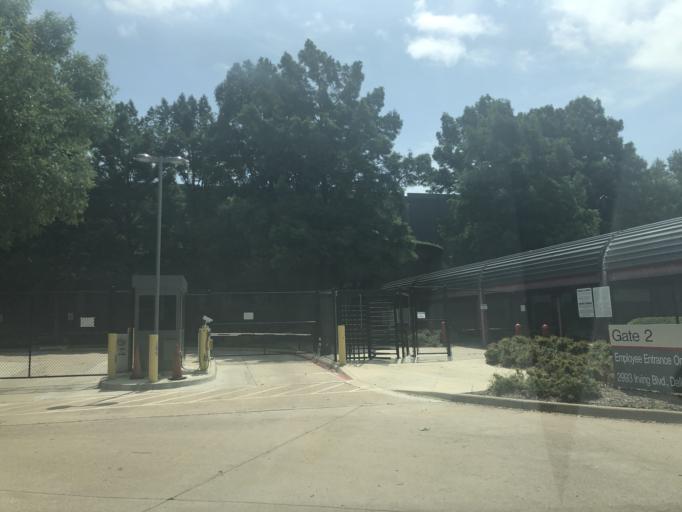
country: US
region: Texas
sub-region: Dallas County
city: Dallas
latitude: 32.8100
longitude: -96.8586
